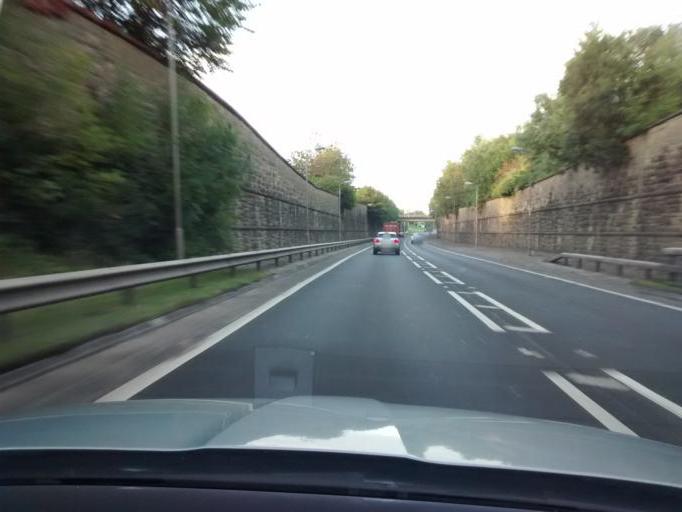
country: GB
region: Scotland
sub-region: Renfrewshire
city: Kilbarchan
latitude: 55.8288
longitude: -4.5376
